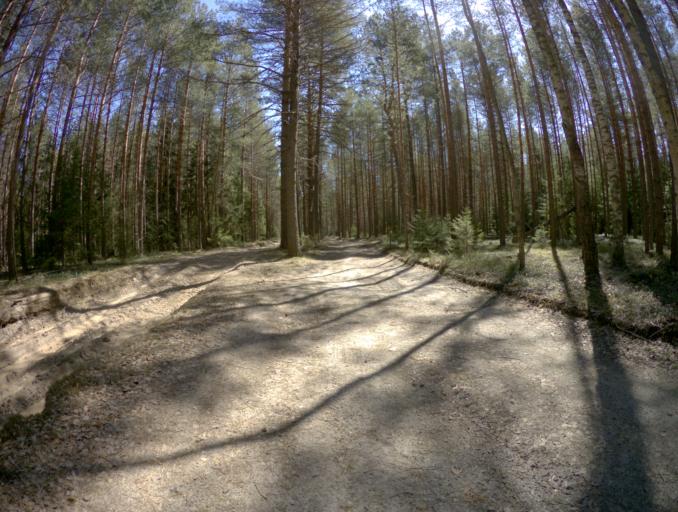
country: RU
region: Vladimir
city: Golovino
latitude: 55.9110
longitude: 40.4378
